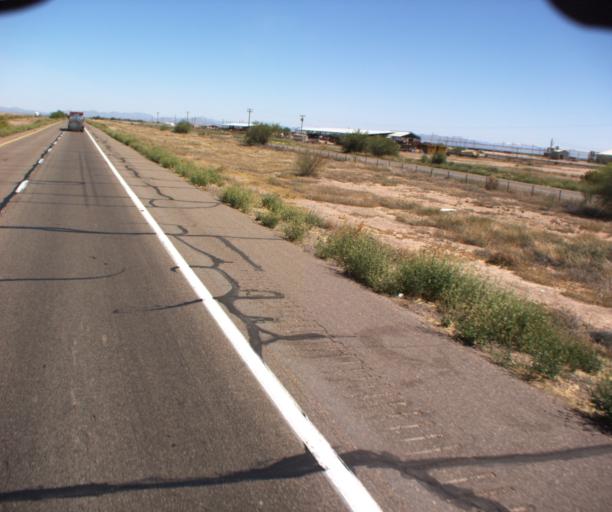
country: US
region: Arizona
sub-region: Maricopa County
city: Gila Bend
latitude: 32.9245
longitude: -112.8666
